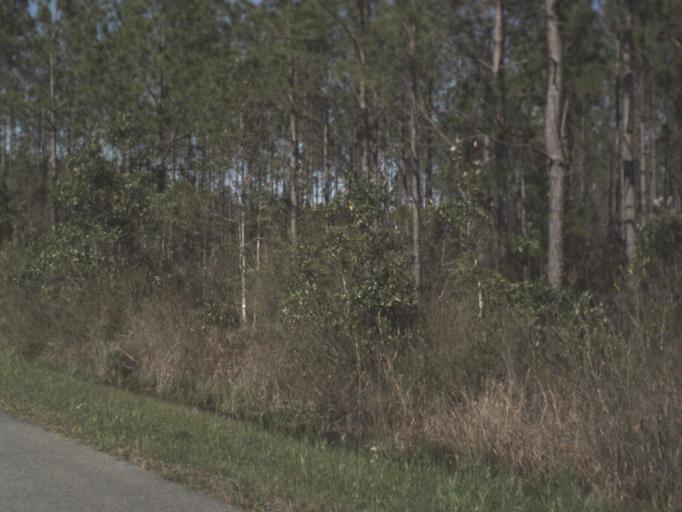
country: US
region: Florida
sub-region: Gulf County
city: Wewahitchka
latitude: 29.9986
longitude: -85.1719
